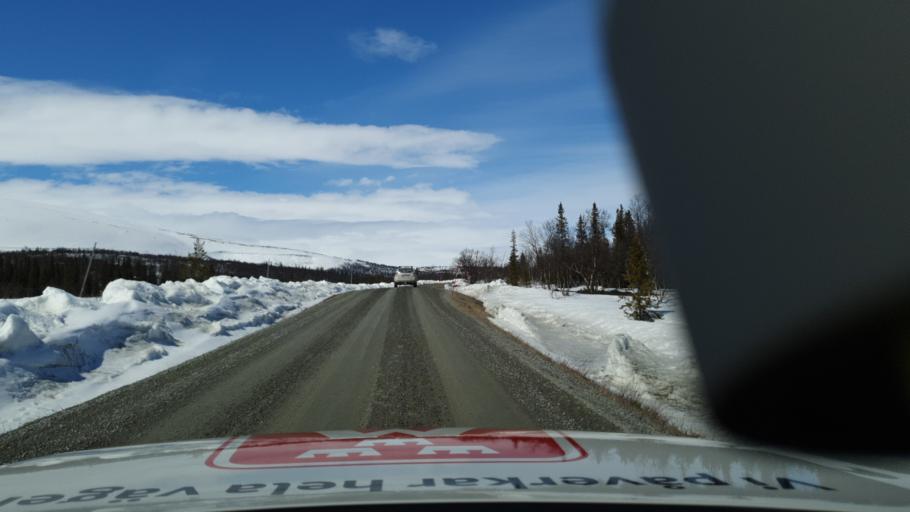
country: SE
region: Jaemtland
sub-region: Are Kommun
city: Are
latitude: 62.8748
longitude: 12.7374
